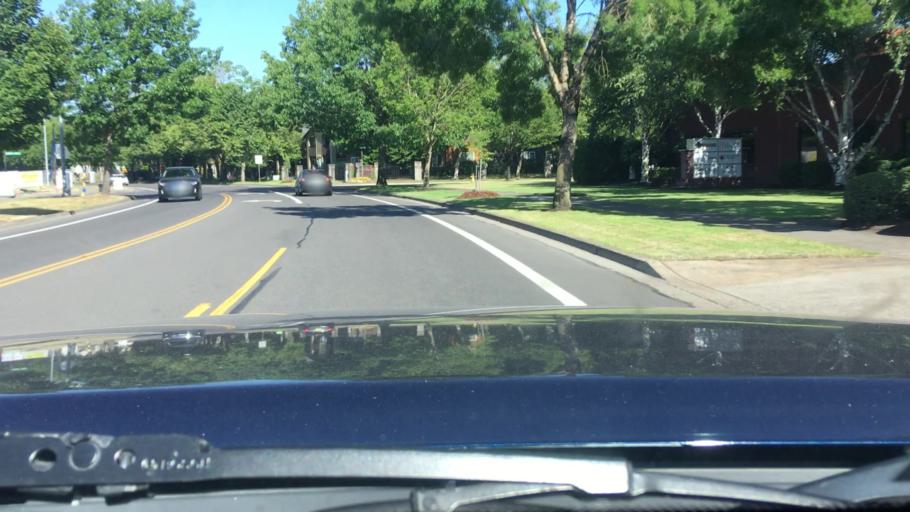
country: US
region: Oregon
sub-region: Lane County
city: Coburg
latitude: 44.0921
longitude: -123.0609
